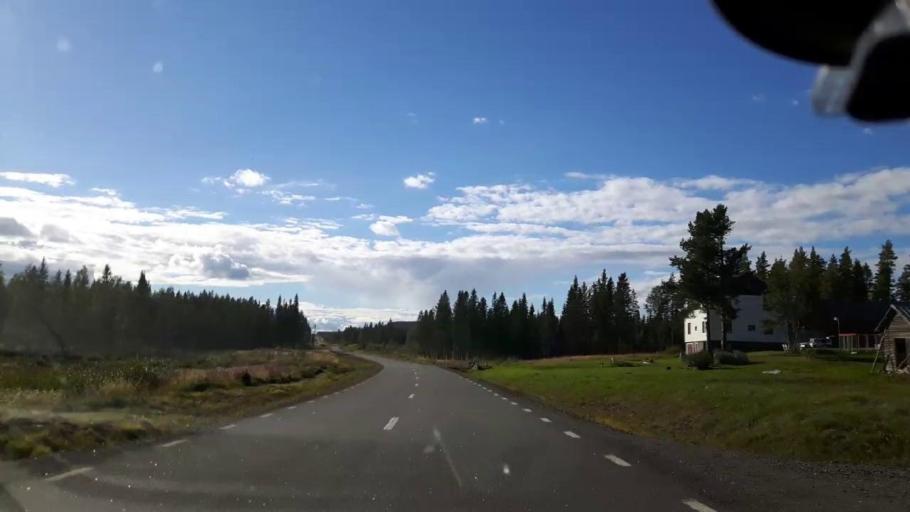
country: SE
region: Jaemtland
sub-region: Stroemsunds Kommun
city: Stroemsund
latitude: 63.5394
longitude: 15.9890
